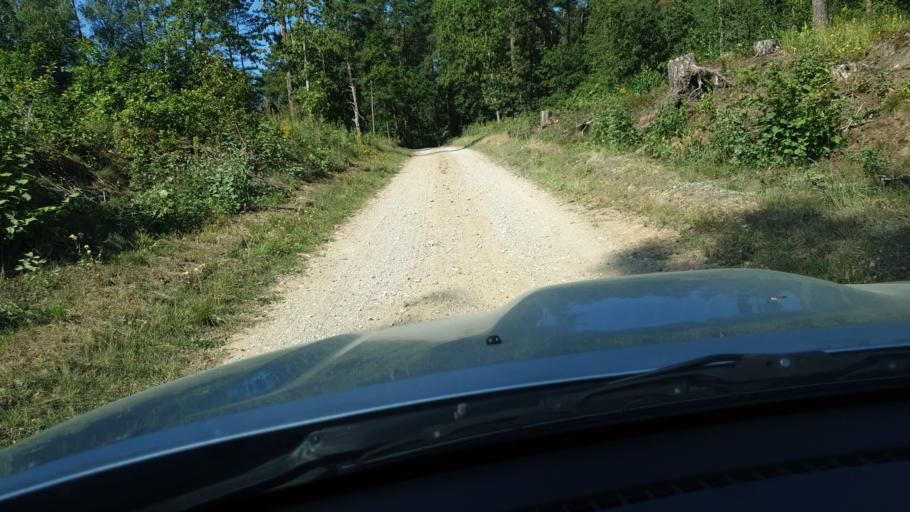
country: LT
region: Vilnius County
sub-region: Vilniaus Rajonas
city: Vievis
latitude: 54.9028
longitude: 24.8815
